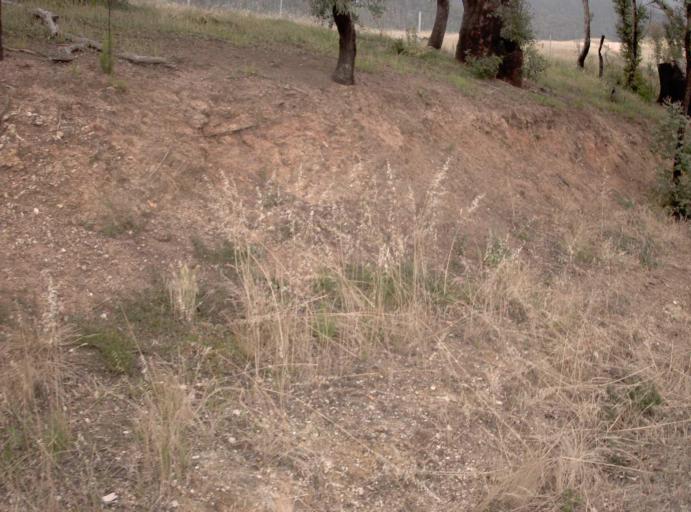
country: AU
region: Victoria
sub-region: Wellington
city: Heyfield
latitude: -37.8263
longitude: 146.6770
